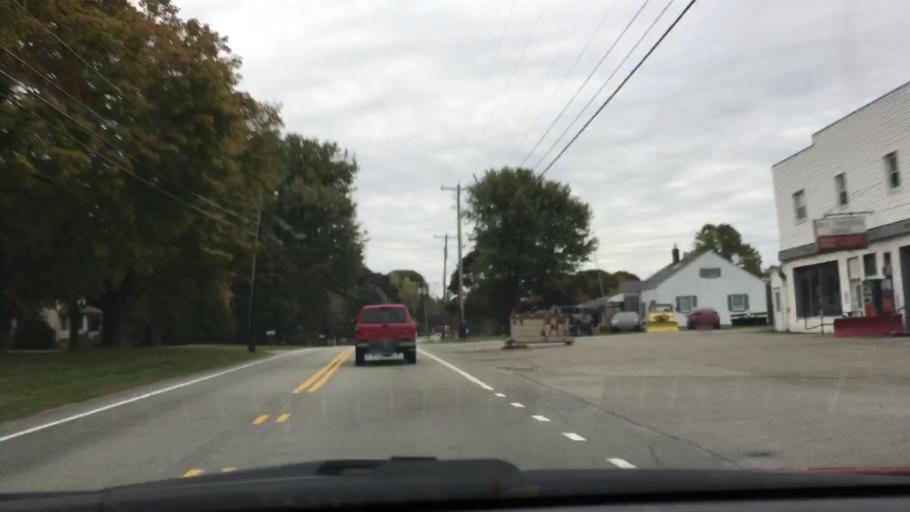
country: US
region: Pennsylvania
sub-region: Armstrong County
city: Orchard Hills
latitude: 40.6081
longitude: -79.4812
